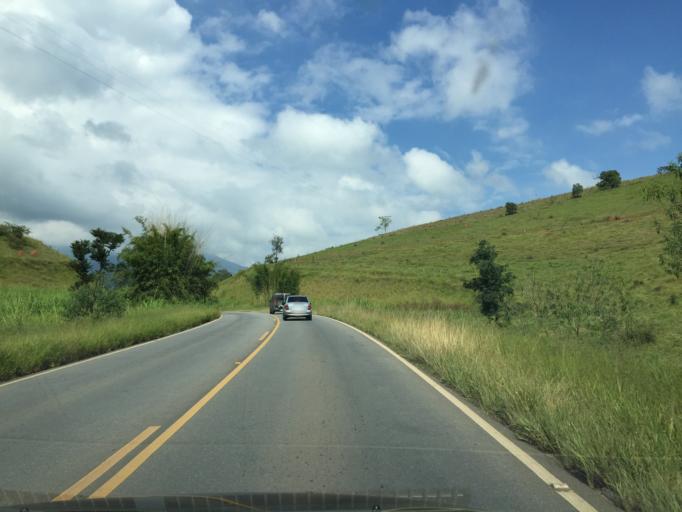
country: BR
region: Minas Gerais
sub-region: Itanhandu
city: Itanhandu
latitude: -22.3226
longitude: -44.9347
